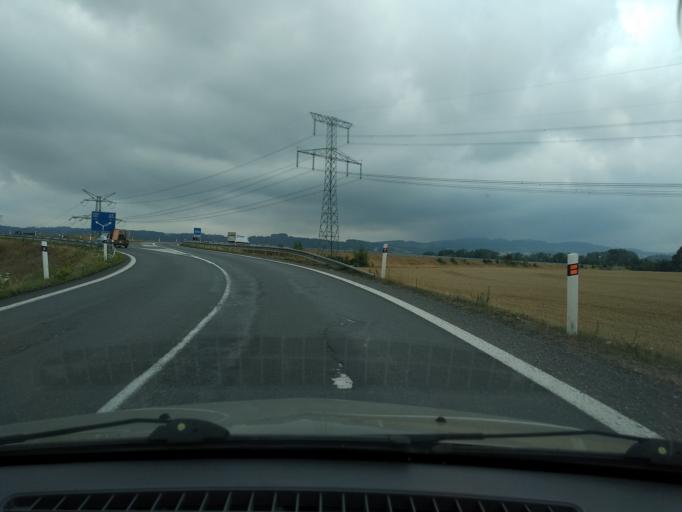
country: CZ
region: Olomoucky
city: Postrelmov
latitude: 49.8944
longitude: 16.8972
